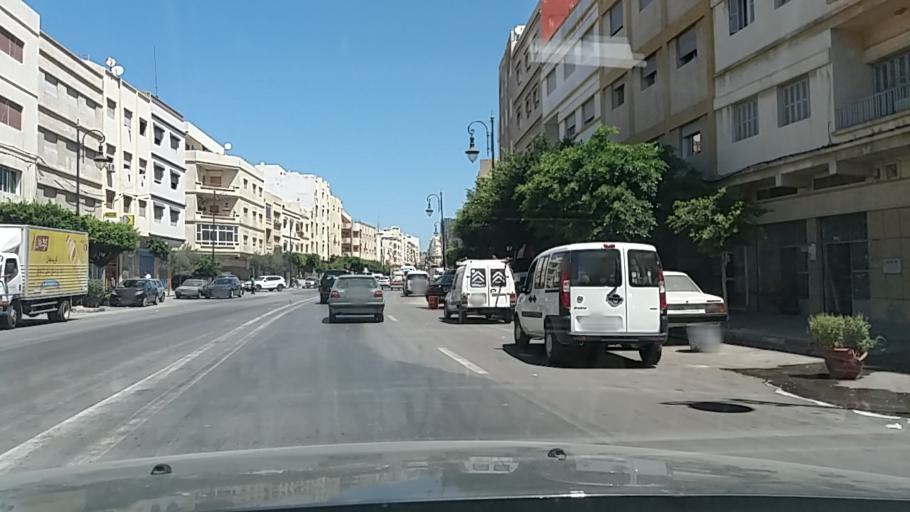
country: MA
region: Tanger-Tetouan
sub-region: Tanger-Assilah
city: Tangier
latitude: 35.7599
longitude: -5.7959
